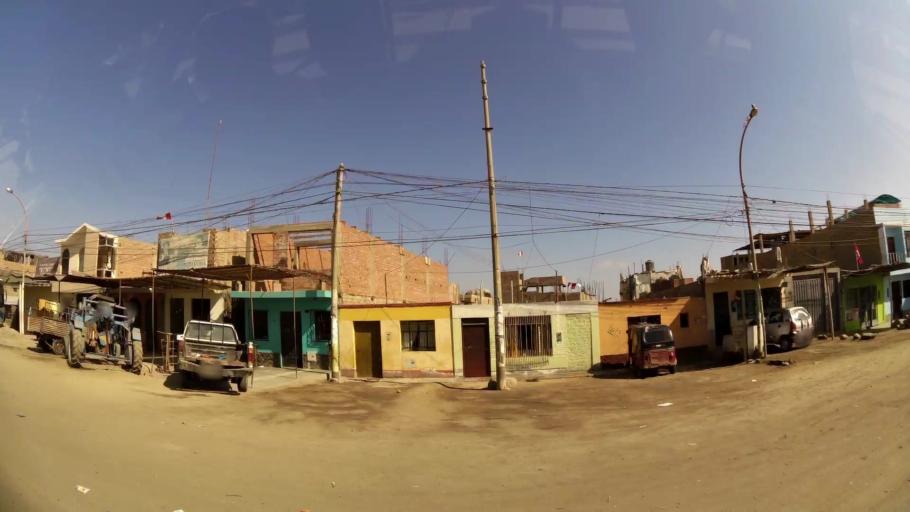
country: PE
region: Ica
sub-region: Provincia de Chincha
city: Chincha Alta
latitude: -13.4109
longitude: -76.1266
